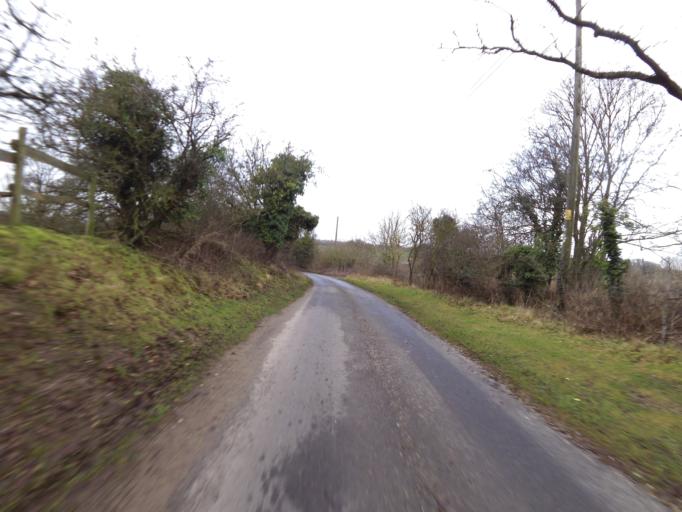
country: GB
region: England
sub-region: Suffolk
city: Needham Market
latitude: 52.1623
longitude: 1.0625
